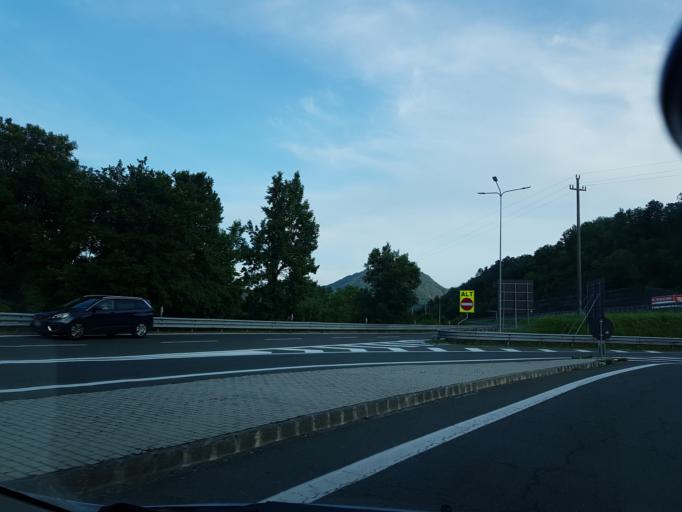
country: IT
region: Tuscany
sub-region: Provincia di Massa-Carrara
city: Terrarossa
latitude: 44.2171
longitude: 9.9614
